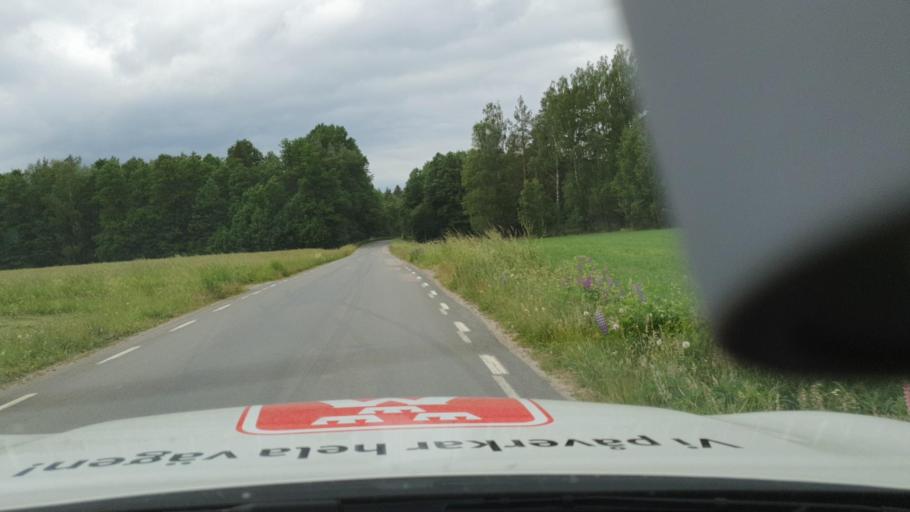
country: SE
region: Vaestra Goetaland
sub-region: Tidaholms Kommun
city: Olofstorp
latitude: 58.1919
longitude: 14.0363
